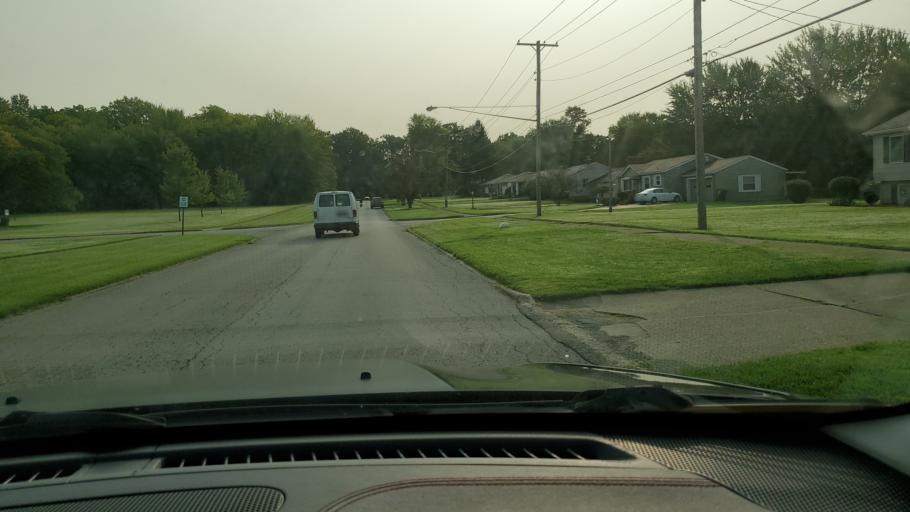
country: US
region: Ohio
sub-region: Mahoning County
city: Poland
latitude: 41.0334
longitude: -80.6190
